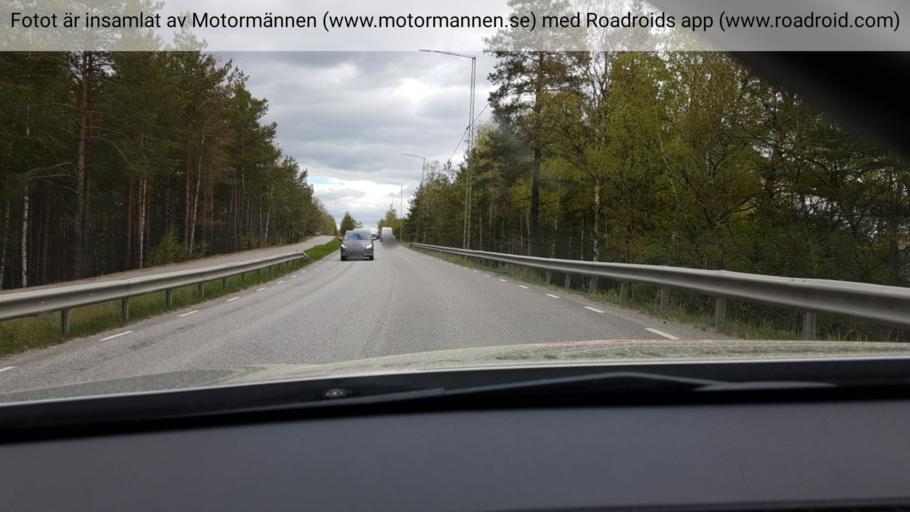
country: SE
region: Stockholm
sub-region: Haninge Kommun
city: Jordbro
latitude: 59.1281
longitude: 18.1156
